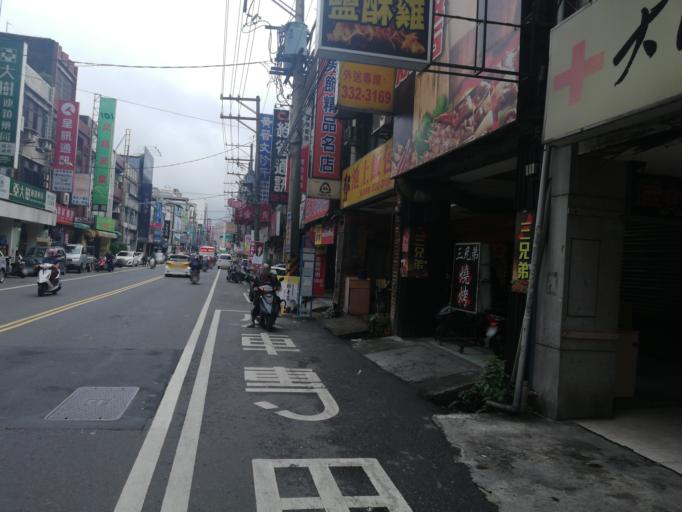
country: TW
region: Taiwan
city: Taoyuan City
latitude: 24.9994
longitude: 121.3081
